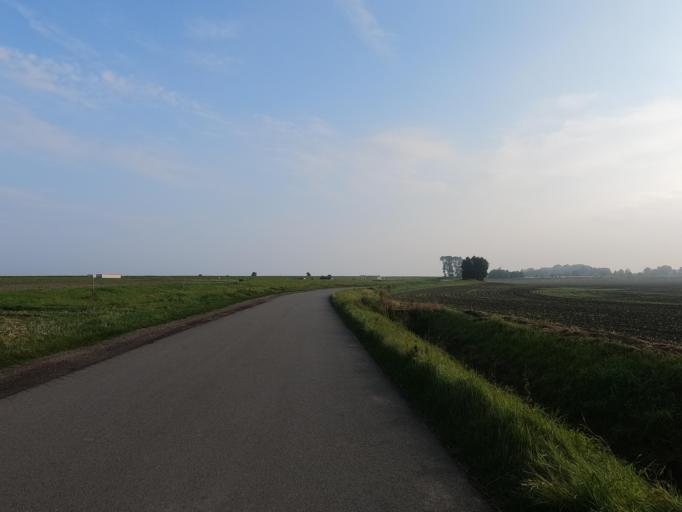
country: DE
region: Schleswig-Holstein
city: Dahme
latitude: 54.2628
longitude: 11.0794
